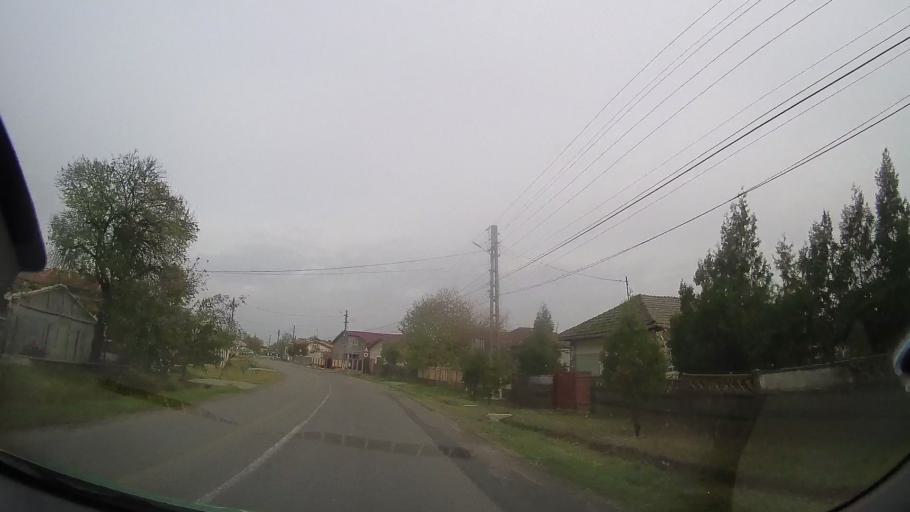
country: RO
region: Prahova
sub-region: Comuna Balta Doamnei
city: Balta Doamnei
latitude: 44.7580
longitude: 26.1703
